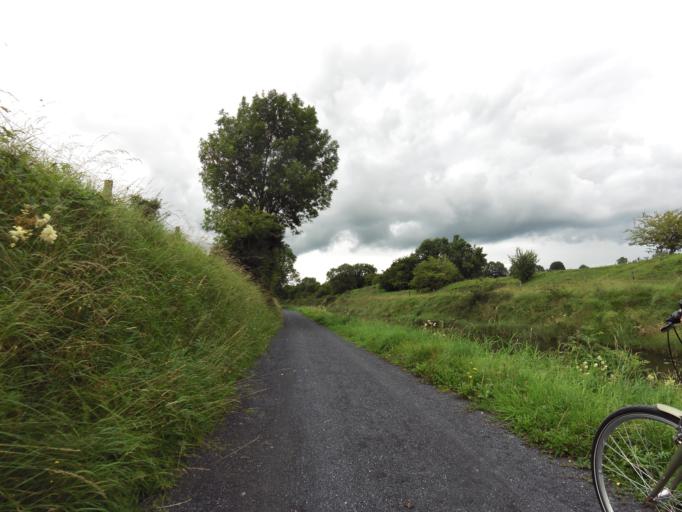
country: IE
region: Leinster
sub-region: An Iarmhi
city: An Muileann gCearr
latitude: 53.5256
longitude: -7.4471
